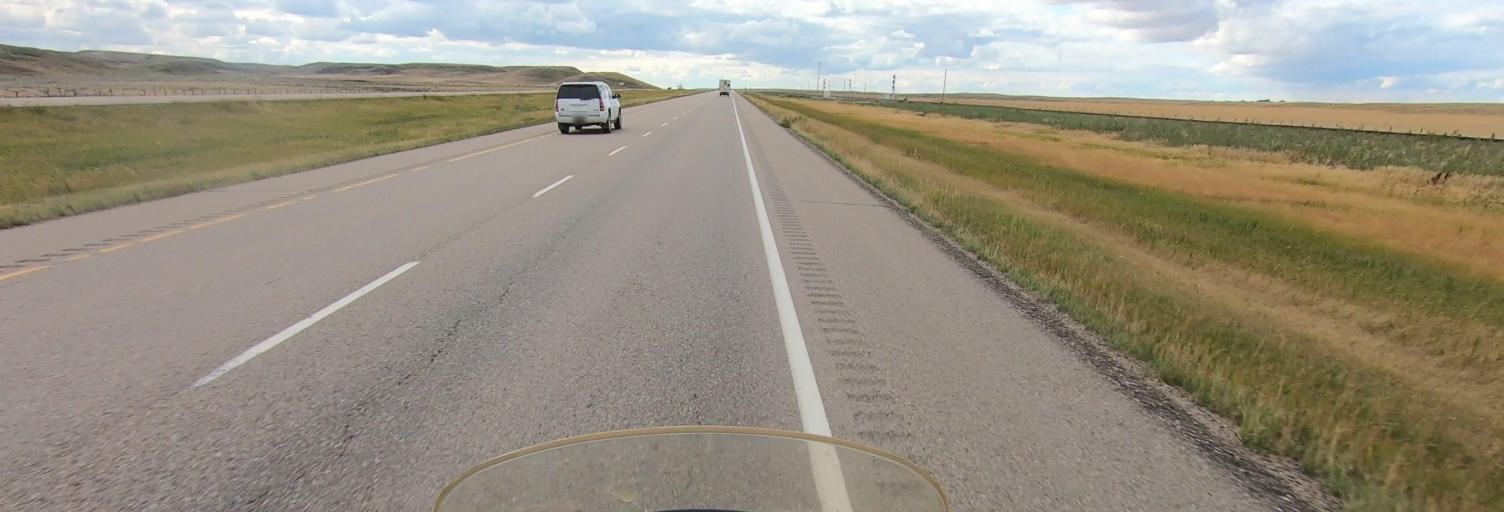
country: CA
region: Alberta
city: Medicine Hat
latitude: 49.9479
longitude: -110.2158
